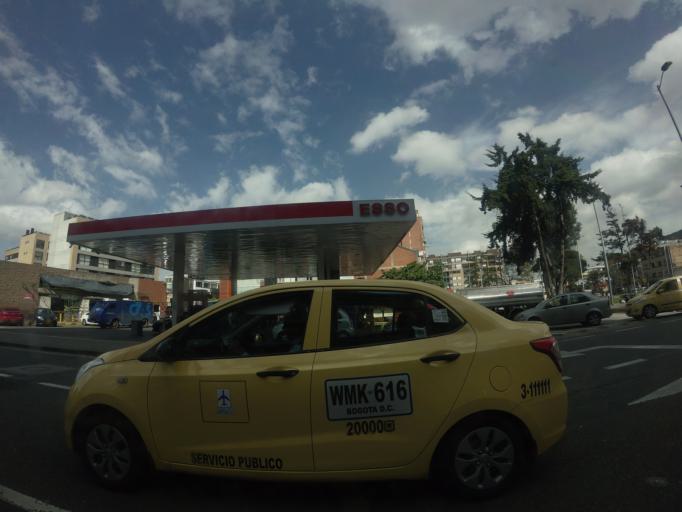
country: CO
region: Bogota D.C.
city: Bogota
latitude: 4.6450
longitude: -74.0615
